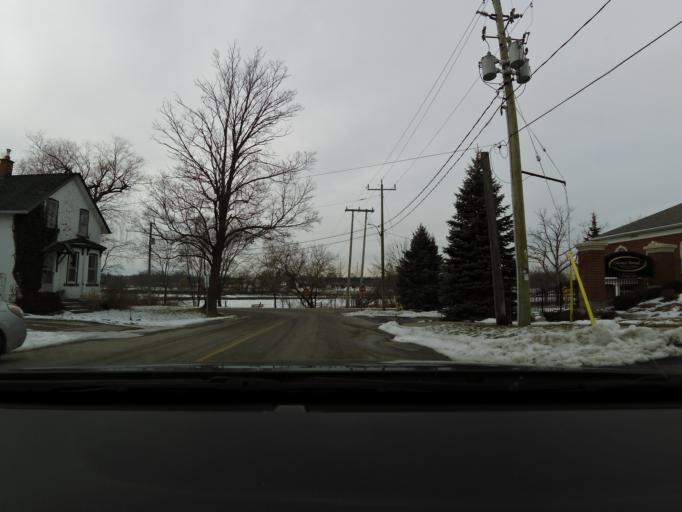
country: CA
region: Ontario
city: Ancaster
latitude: 42.9505
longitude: -79.8592
